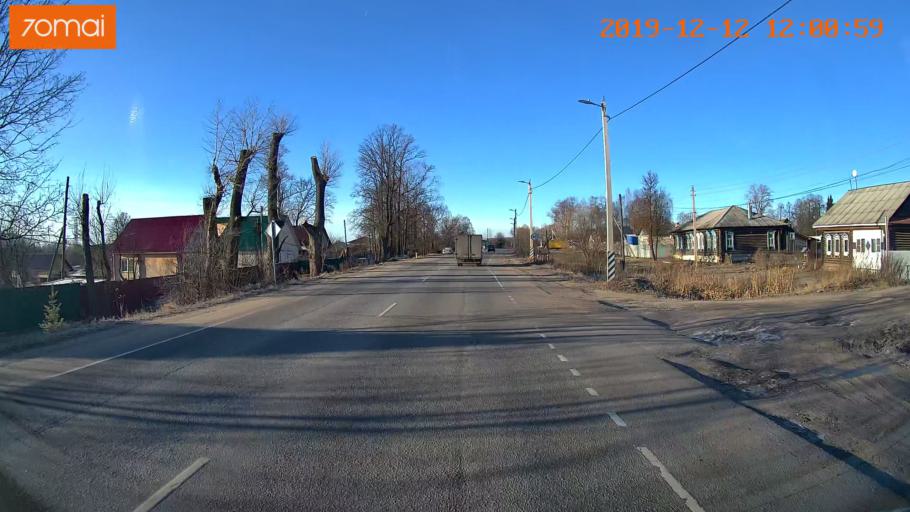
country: RU
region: Ivanovo
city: Kitovo
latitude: 56.8639
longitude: 41.2933
